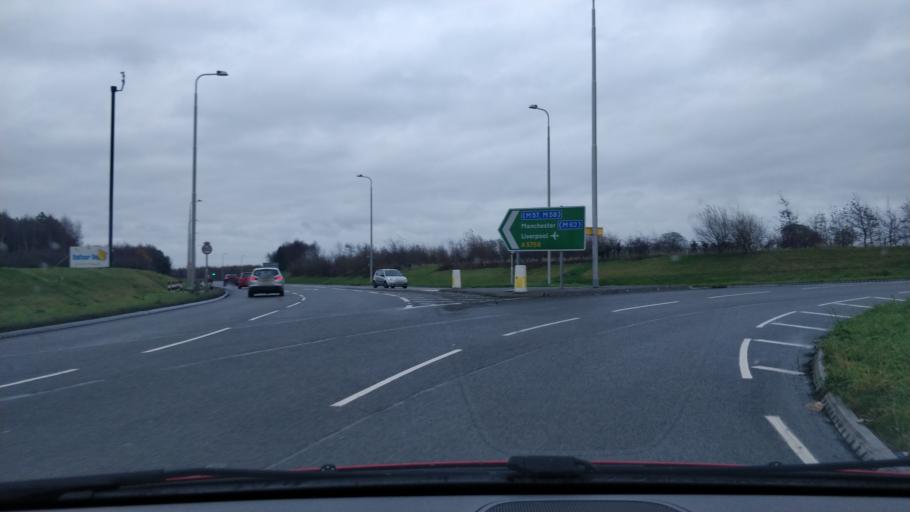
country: GB
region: England
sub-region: Sefton
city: Thornton
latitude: 53.5048
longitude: -3.0017
